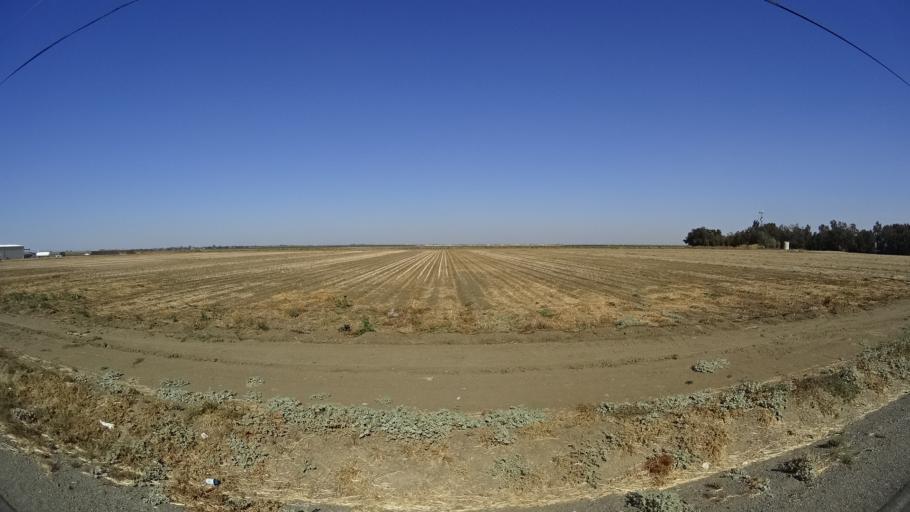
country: US
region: California
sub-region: Yolo County
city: Woodland
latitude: 38.6190
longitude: -121.7459
